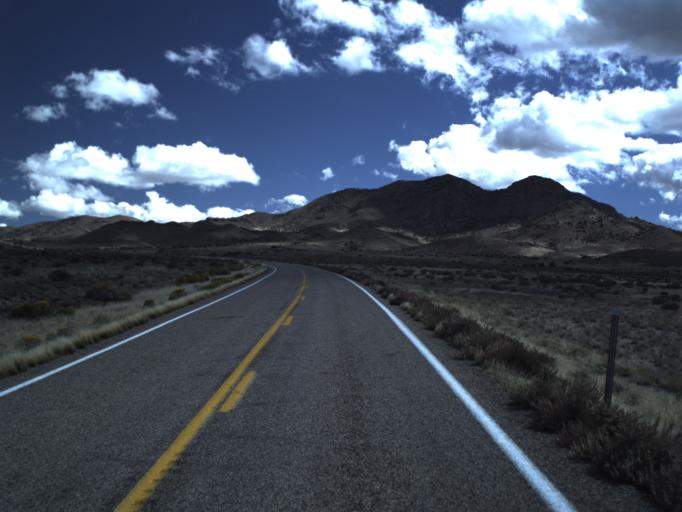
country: US
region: Utah
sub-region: Beaver County
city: Milford
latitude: 38.4383
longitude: -113.3119
